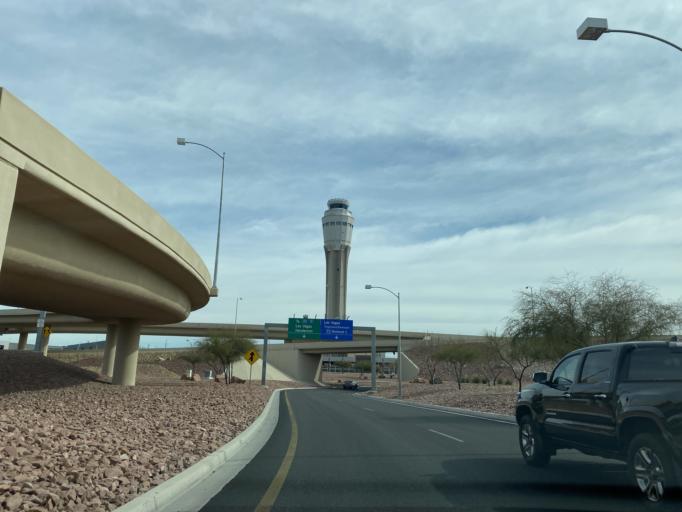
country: US
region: Nevada
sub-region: Clark County
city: Paradise
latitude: 36.0867
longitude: -115.1444
